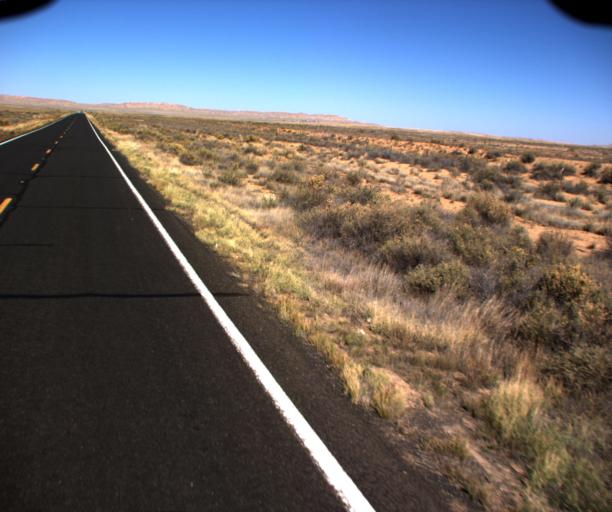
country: US
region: Arizona
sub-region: Navajo County
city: First Mesa
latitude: 35.6905
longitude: -110.5039
